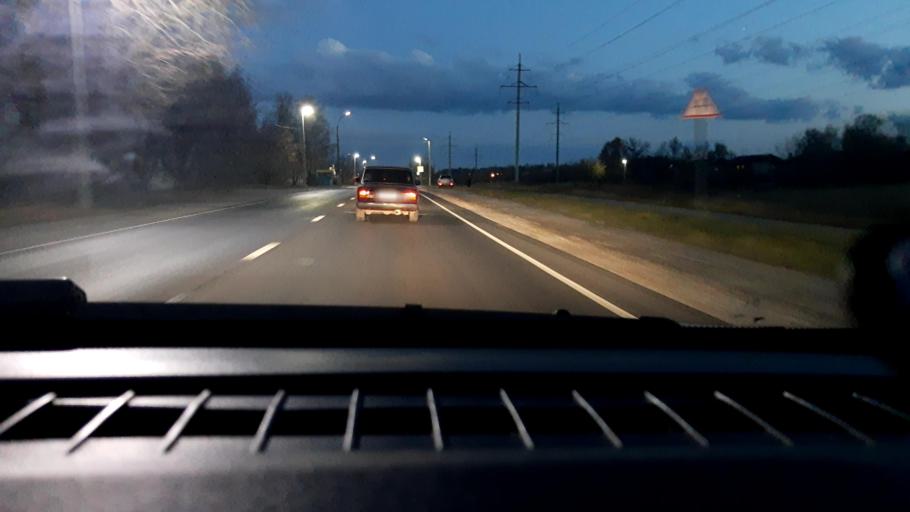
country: RU
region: Nizjnij Novgorod
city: Novaya Balakhna
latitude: 56.4812
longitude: 43.6027
